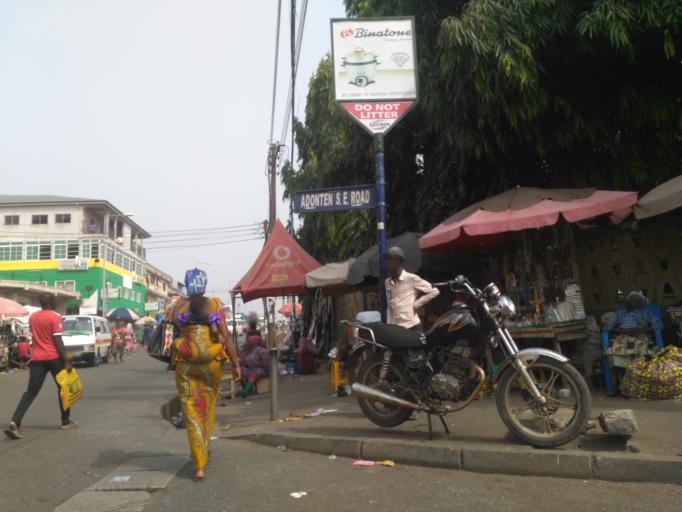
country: GH
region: Ashanti
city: Kumasi
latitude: 6.6955
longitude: -1.6187
